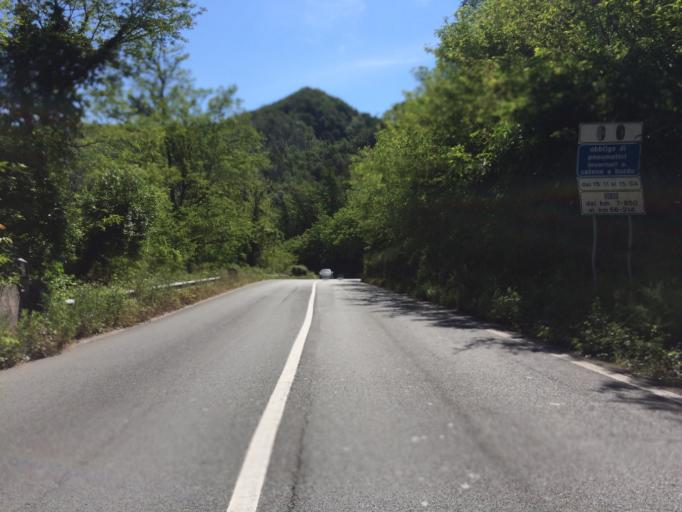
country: IT
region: Tuscany
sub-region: Provincia di Massa-Carrara
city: Albiano Magra
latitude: 44.1838
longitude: 9.9312
